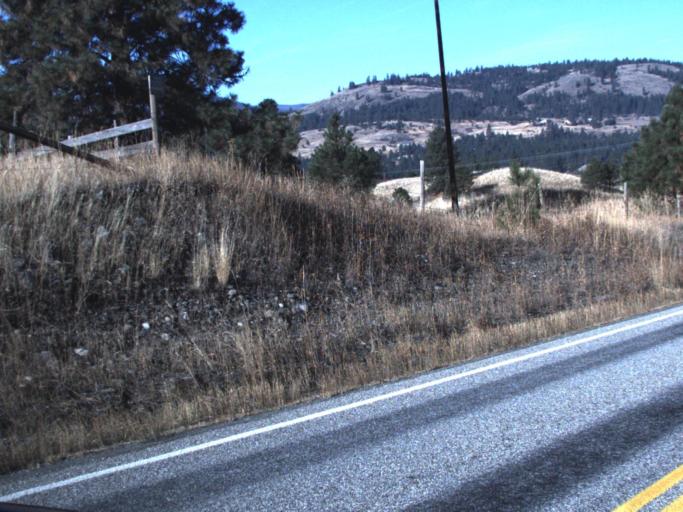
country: US
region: Washington
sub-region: Ferry County
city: Republic
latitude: 48.7317
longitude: -118.6551
